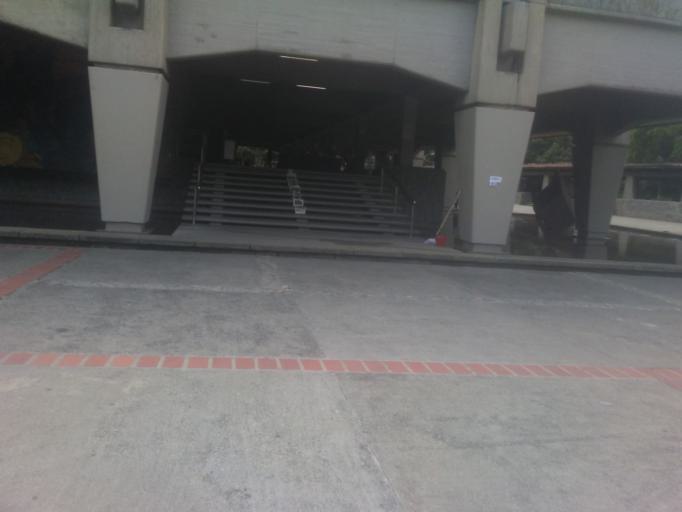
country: CO
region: Antioquia
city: Medellin
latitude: 6.2673
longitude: -75.5691
